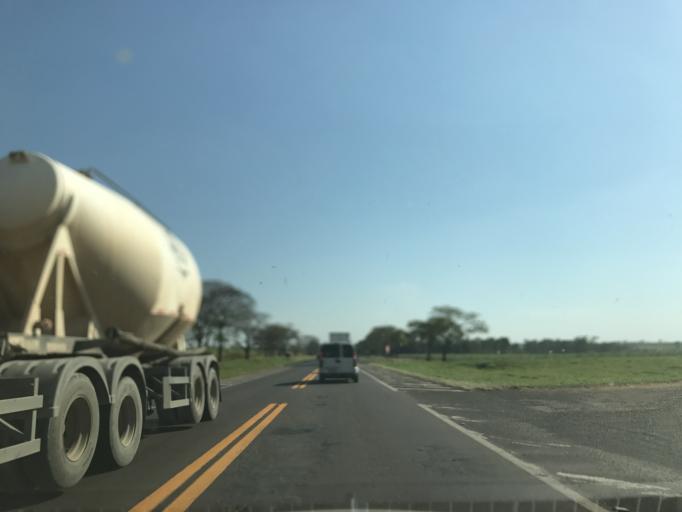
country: BR
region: Sao Paulo
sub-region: Penapolis
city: Penapolis
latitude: -21.4757
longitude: -50.1960
